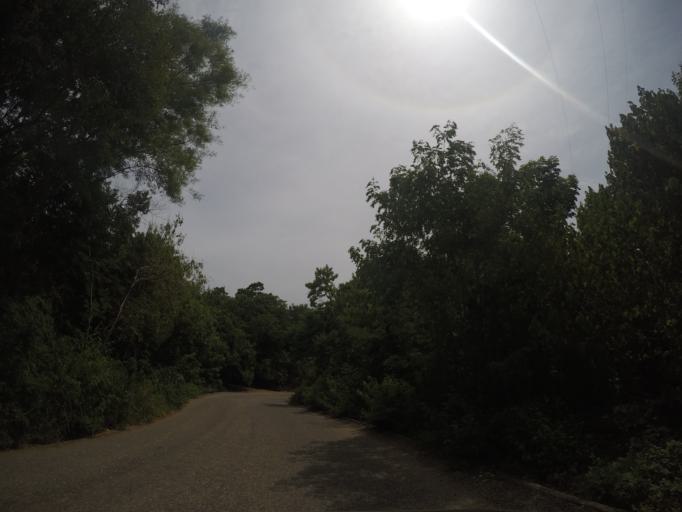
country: MX
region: Oaxaca
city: Santa Maria Tonameca
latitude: 15.6663
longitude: -96.5302
